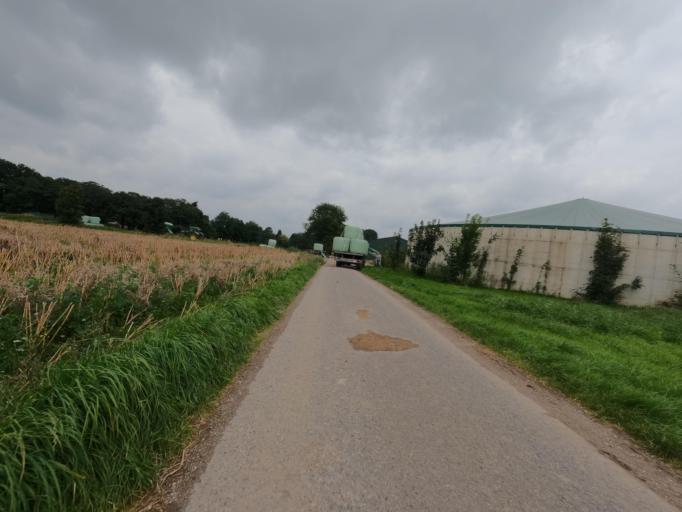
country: DE
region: North Rhine-Westphalia
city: Baesweiler
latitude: 50.9466
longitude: 6.1649
